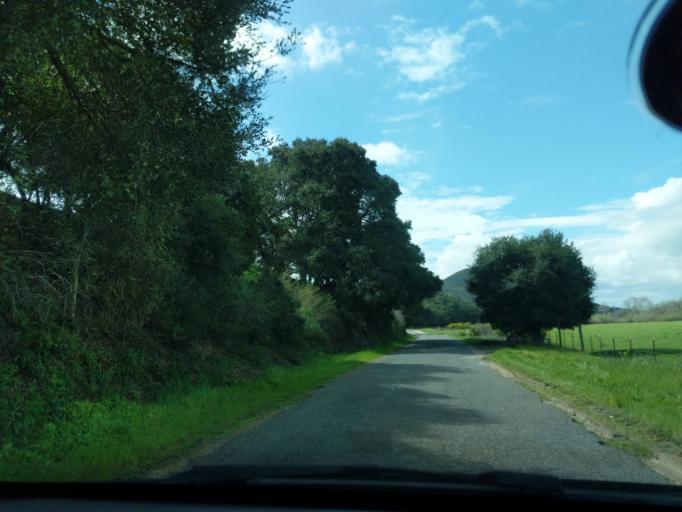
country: US
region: California
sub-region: San Benito County
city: San Juan Bautista
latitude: 36.7852
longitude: -121.5815
